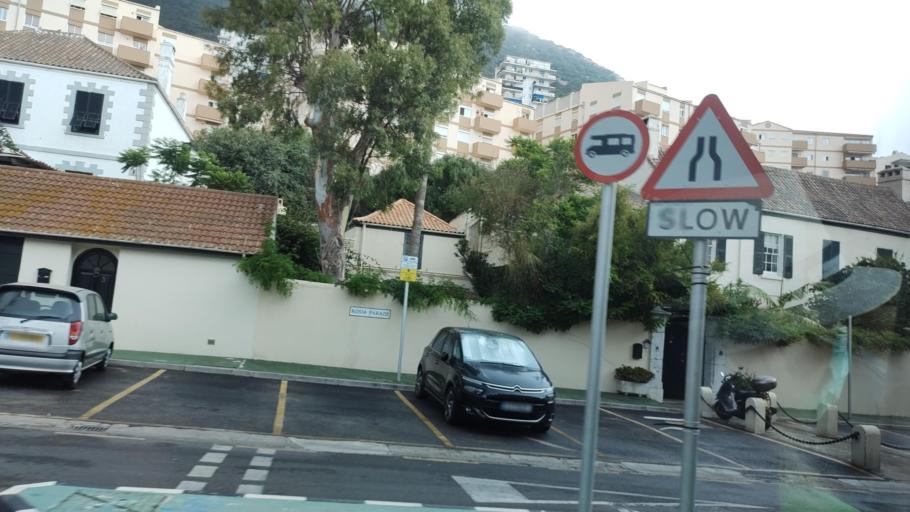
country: GI
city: Gibraltar
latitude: 36.1224
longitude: -5.3521
